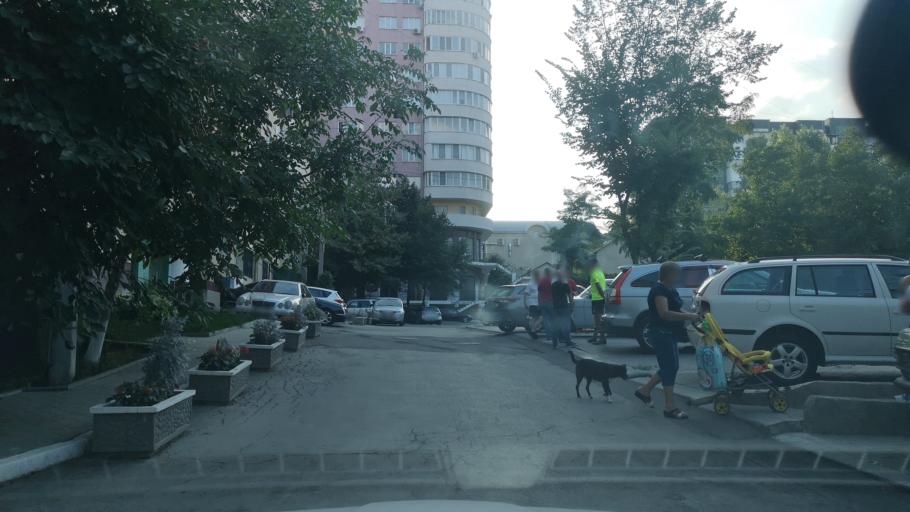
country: MD
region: Chisinau
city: Stauceni
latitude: 47.0480
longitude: 28.8931
